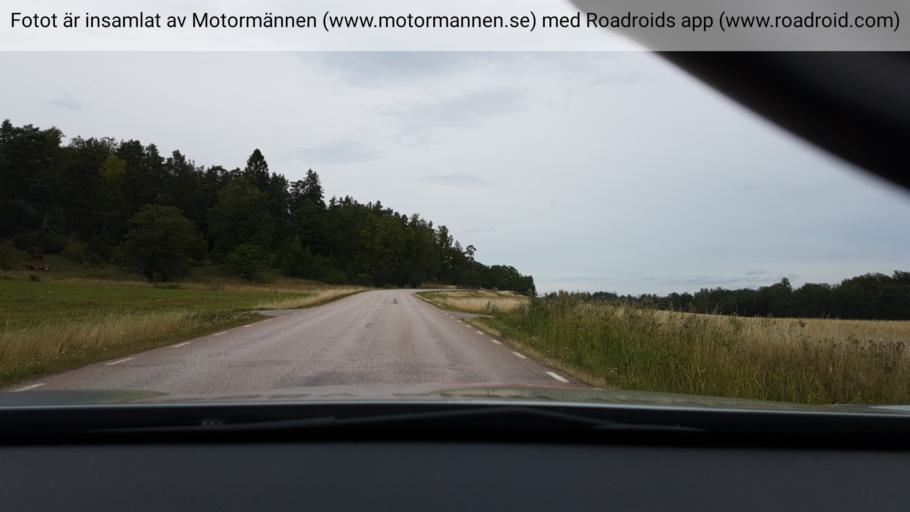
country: SE
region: Soedermanland
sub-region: Gnesta Kommun
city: Gnesta
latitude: 58.9873
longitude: 17.3340
